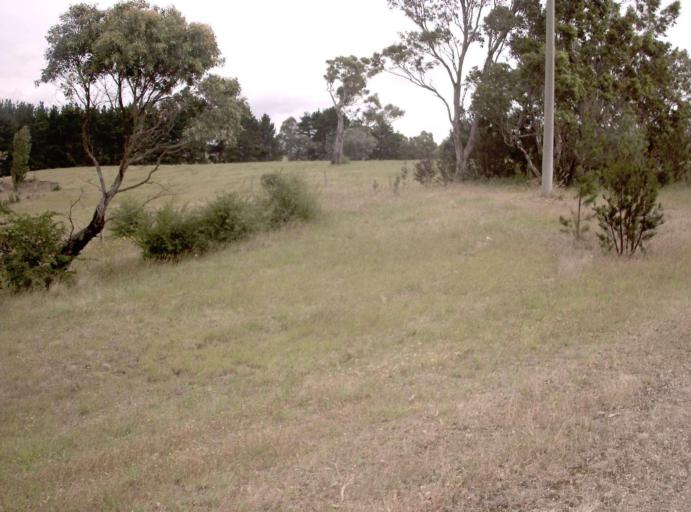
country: AU
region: Victoria
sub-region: Wellington
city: Sale
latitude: -37.9418
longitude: 147.0924
